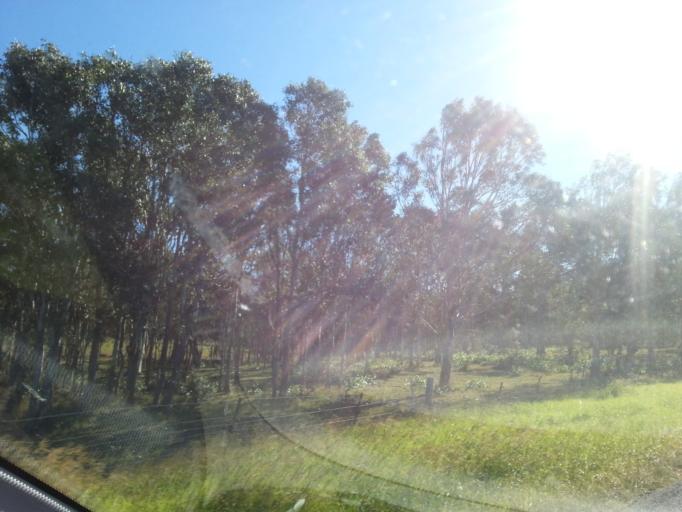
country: AU
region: New South Wales
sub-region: Wollongong
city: Dapto
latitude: -34.5214
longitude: 150.7792
